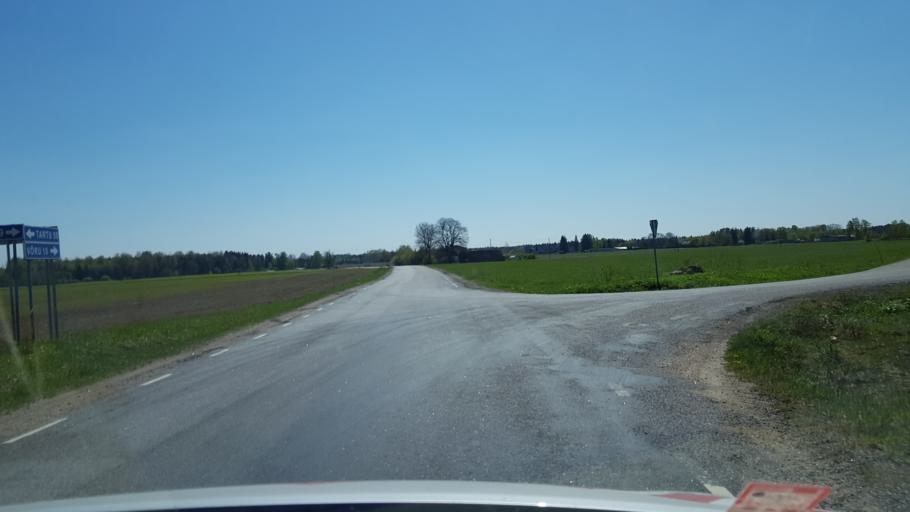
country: EE
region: Vorumaa
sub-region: Voru linn
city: Voru
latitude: 57.9216
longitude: 26.9511
